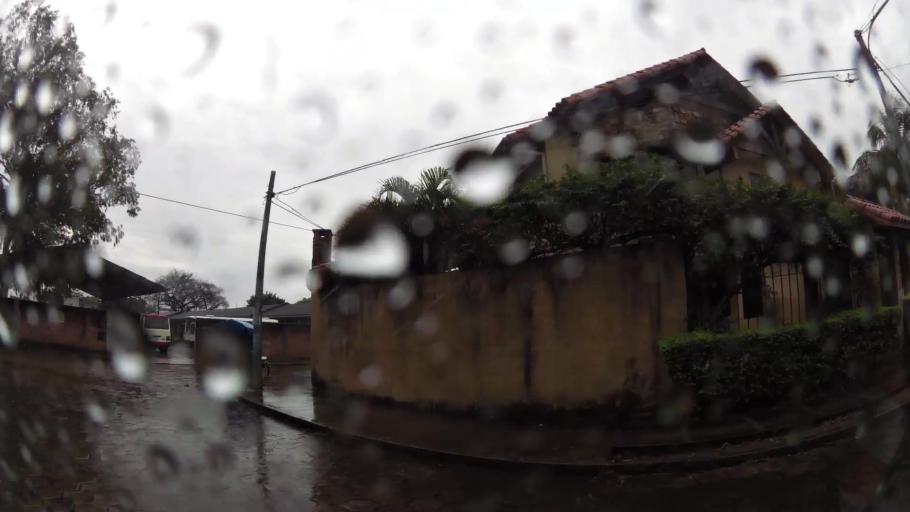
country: BO
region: Santa Cruz
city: Santa Cruz de la Sierra
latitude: -17.7989
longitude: -63.1659
